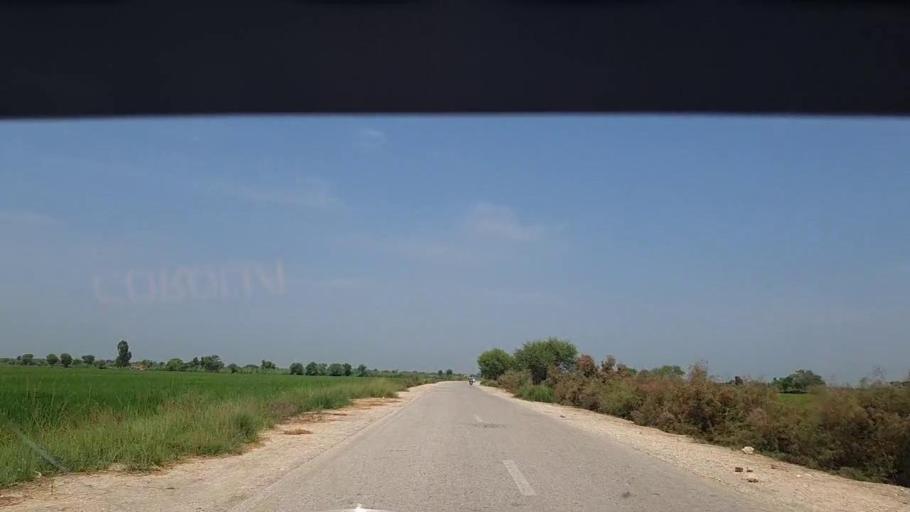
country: PK
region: Sindh
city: Thul
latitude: 28.1329
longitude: 68.8178
